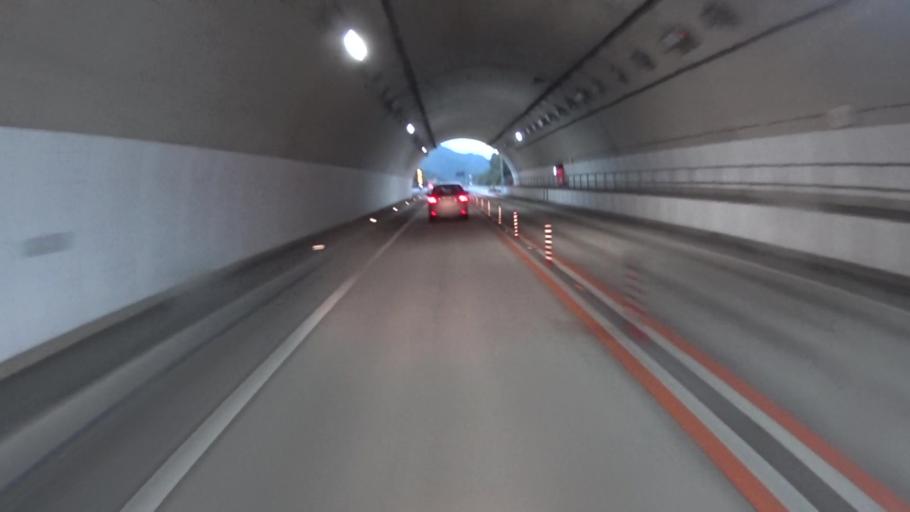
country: JP
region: Kyoto
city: Ayabe
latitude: 35.3027
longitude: 135.3299
